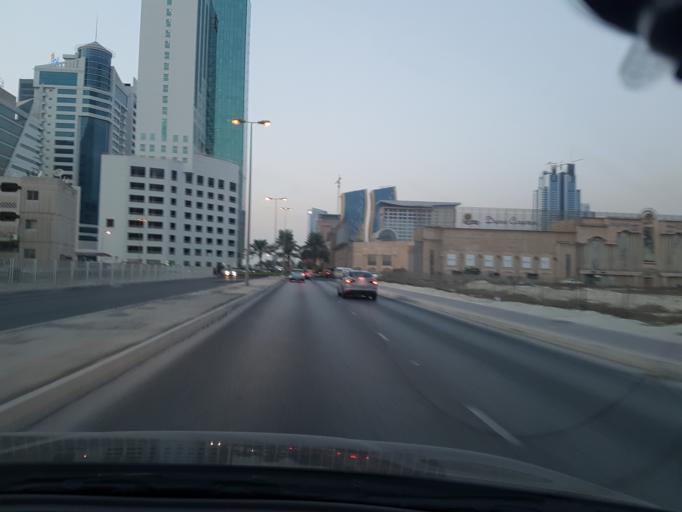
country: BH
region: Manama
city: Jidd Hafs
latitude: 26.2279
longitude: 50.5517
